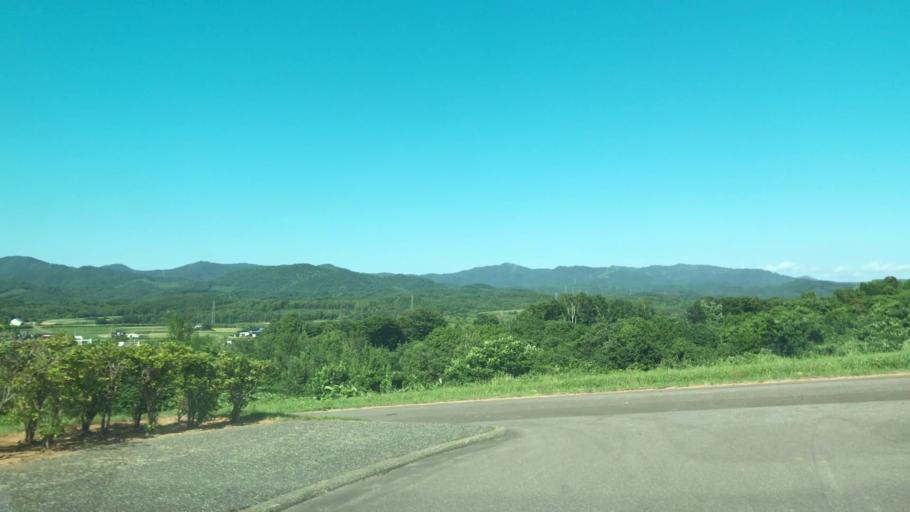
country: JP
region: Hokkaido
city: Iwanai
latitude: 42.9751
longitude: 140.6097
